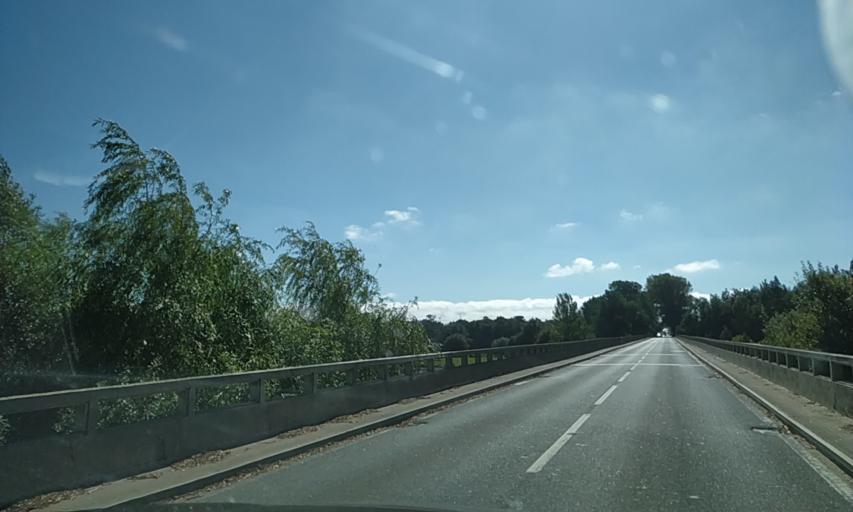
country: PT
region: Aveiro
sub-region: Aveiro
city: Eixo
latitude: 40.6816
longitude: -8.5804
